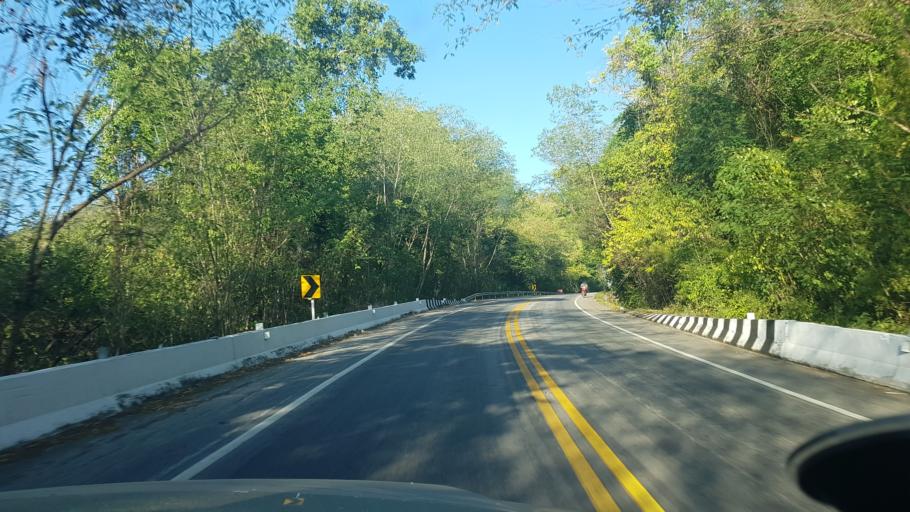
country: TH
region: Khon Kaen
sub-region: Amphoe Phu Pha Man
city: Phu Pha Man
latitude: 16.6458
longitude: 101.7905
